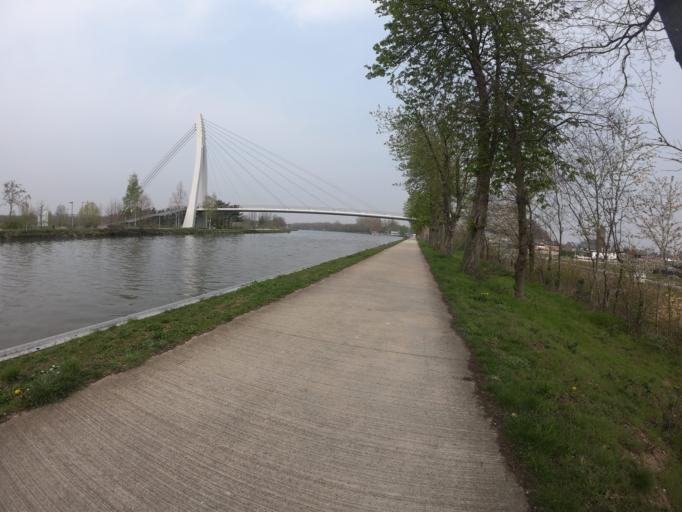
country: BE
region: Flanders
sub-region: Provincie Limburg
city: Maasmechelen
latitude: 51.0119
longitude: 5.7162
